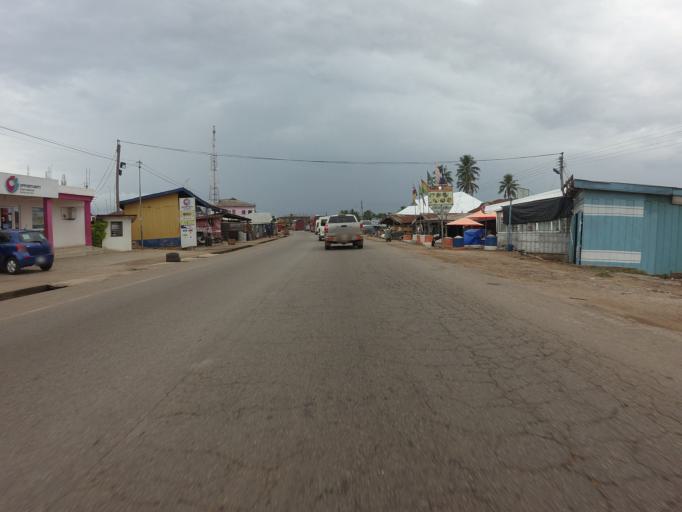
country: GH
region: Ashanti
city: Konongo
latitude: 6.6251
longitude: -1.2062
